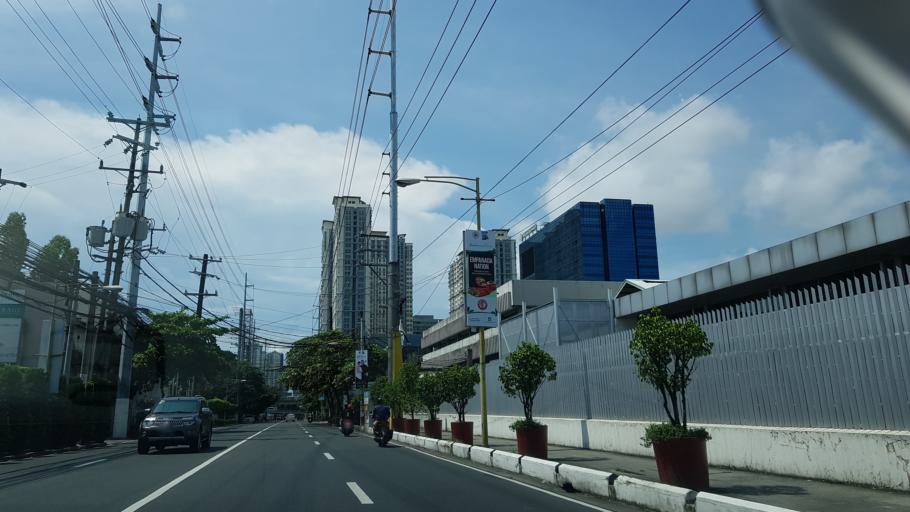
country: PH
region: Metro Manila
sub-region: Makati City
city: Makati City
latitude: 14.5387
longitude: 121.0197
